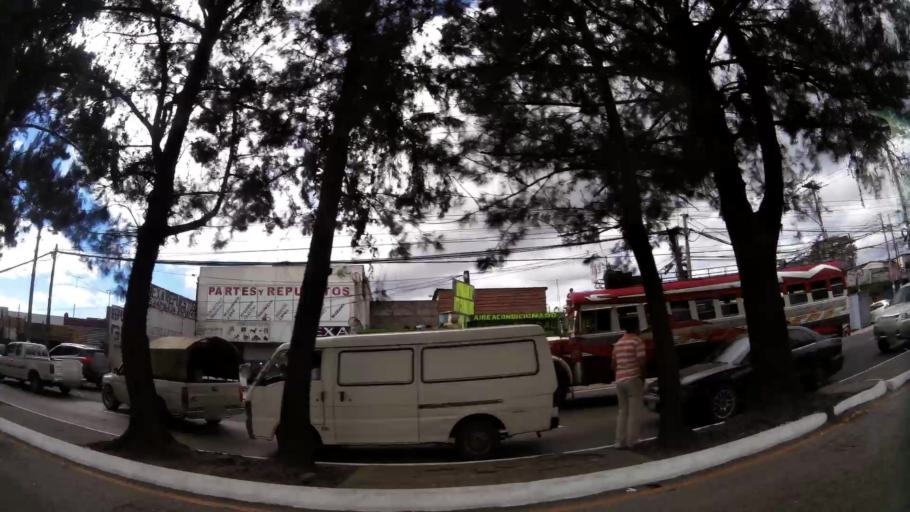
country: GT
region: Guatemala
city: Guatemala City
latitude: 14.6234
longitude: -90.5483
